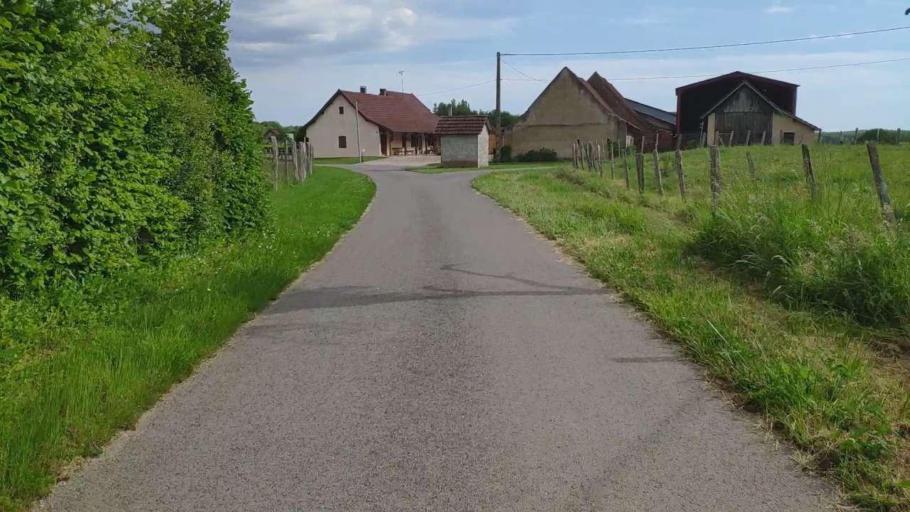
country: FR
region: Bourgogne
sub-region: Departement de Saone-et-Loire
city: Pierre-de-Bresse
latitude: 46.8223
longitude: 5.3388
